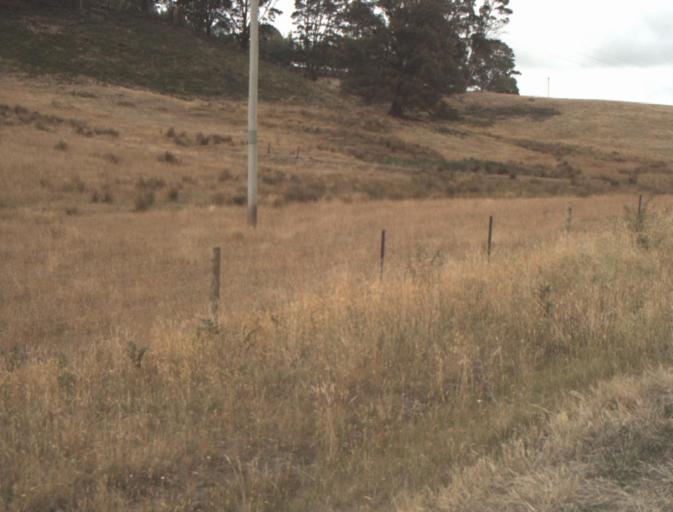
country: AU
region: Tasmania
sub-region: Northern Midlands
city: Evandale
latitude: -41.5187
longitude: 147.4699
